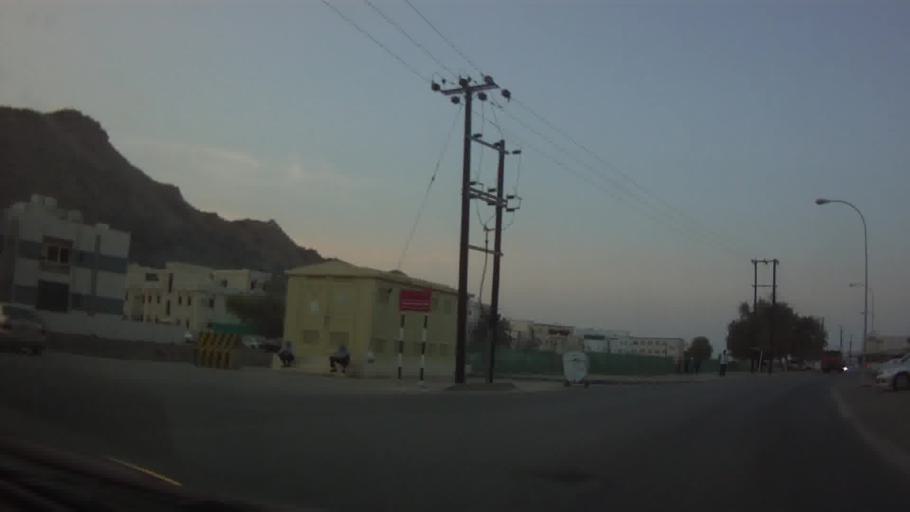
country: OM
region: Muhafazat Masqat
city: Muscat
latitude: 23.6249
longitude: 58.5411
